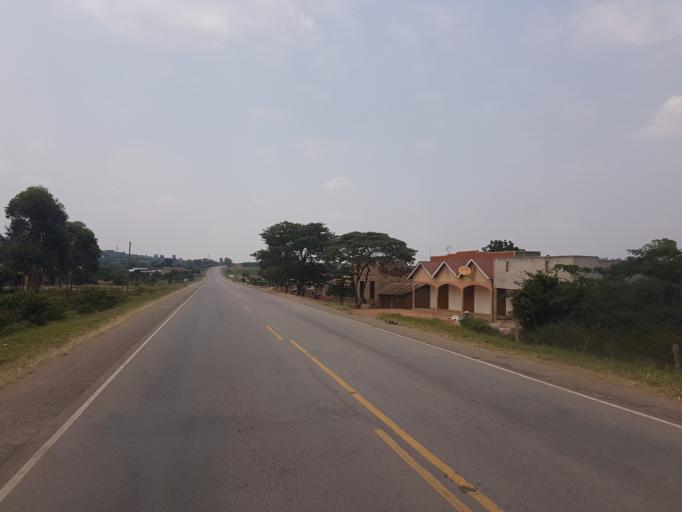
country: UG
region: Western Region
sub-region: Mbarara District
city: Mbarara
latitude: -0.5190
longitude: 30.7492
